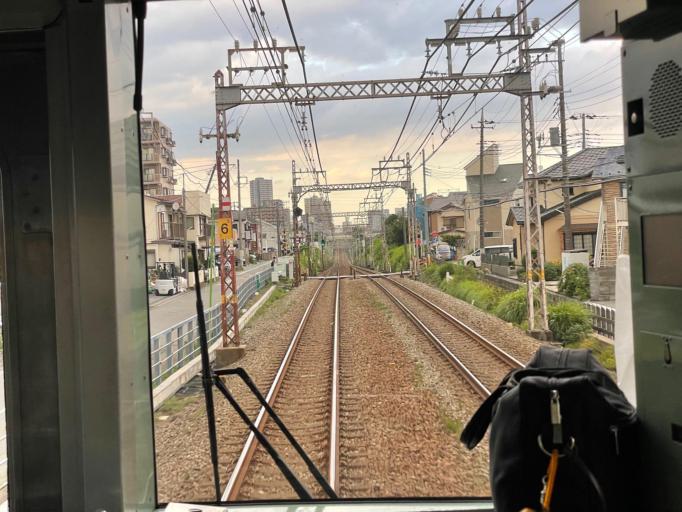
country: JP
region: Kanagawa
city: Zama
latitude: 35.5032
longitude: 139.4121
